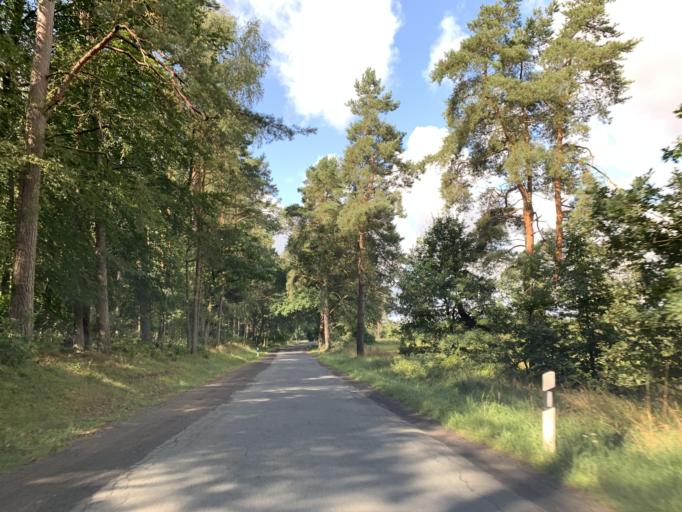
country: DE
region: Mecklenburg-Vorpommern
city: Carpin
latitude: 53.3820
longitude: 13.1984
